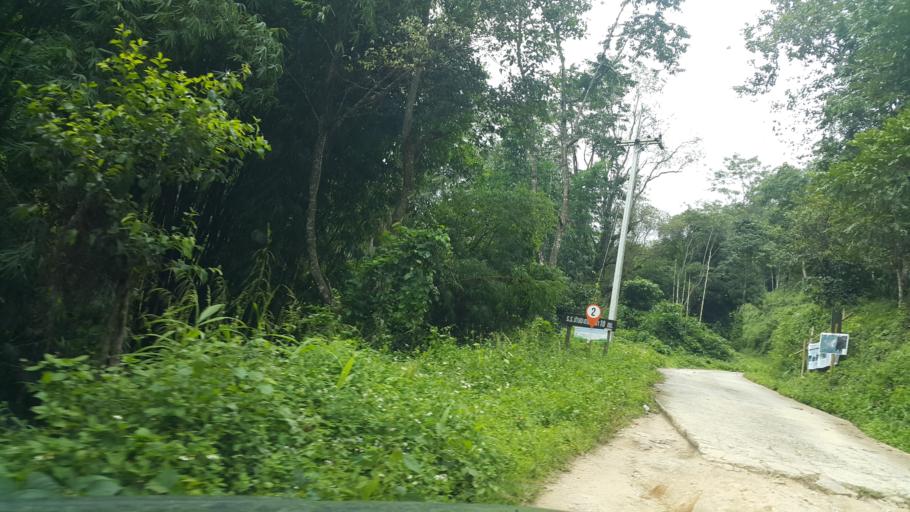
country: TH
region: Lampang
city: Wang Nuea
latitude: 19.0927
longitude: 99.3707
